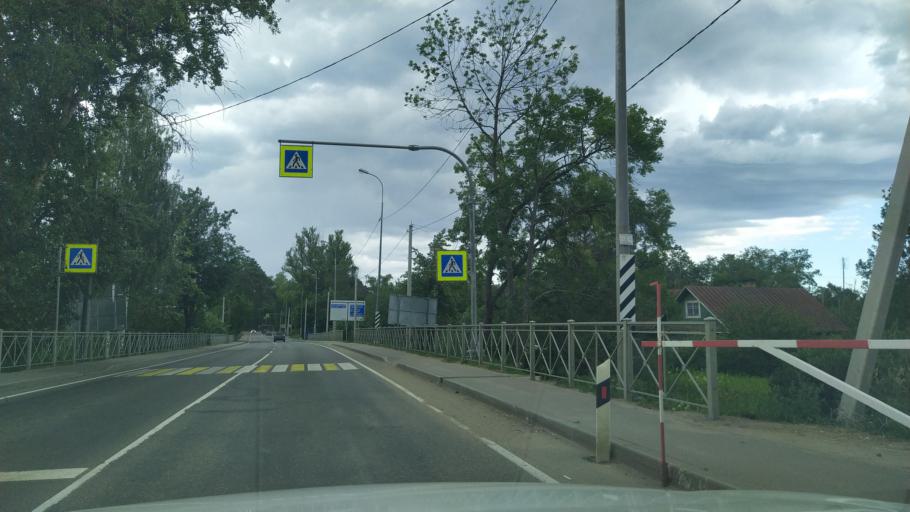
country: RU
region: St.-Petersburg
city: Bol'shaya Izhora
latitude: 59.9384
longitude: 29.5760
